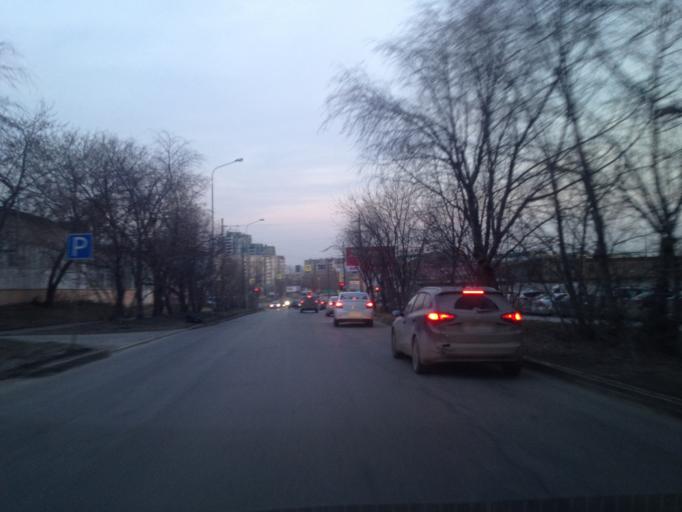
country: RU
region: Sverdlovsk
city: Yekaterinburg
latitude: 56.8330
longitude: 60.6624
